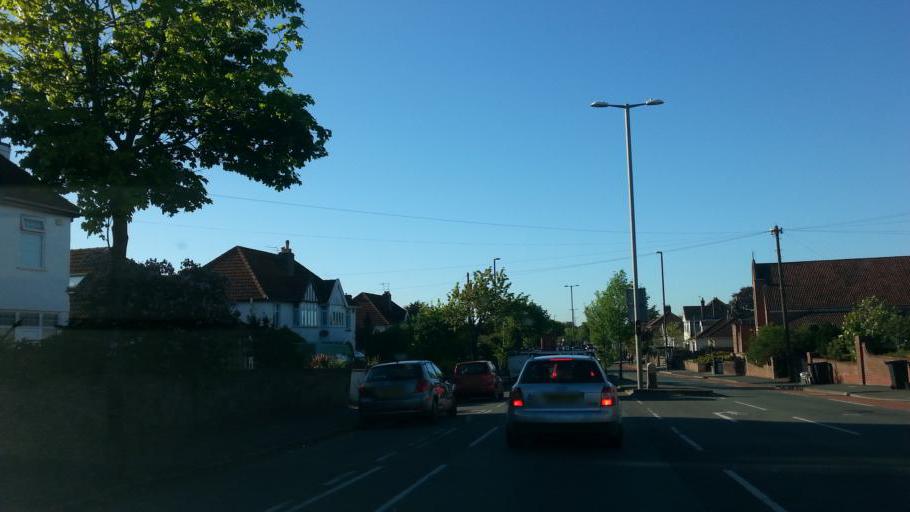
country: GB
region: England
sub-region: Bath and North East Somerset
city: Whitchurch
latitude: 51.4162
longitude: -2.5601
